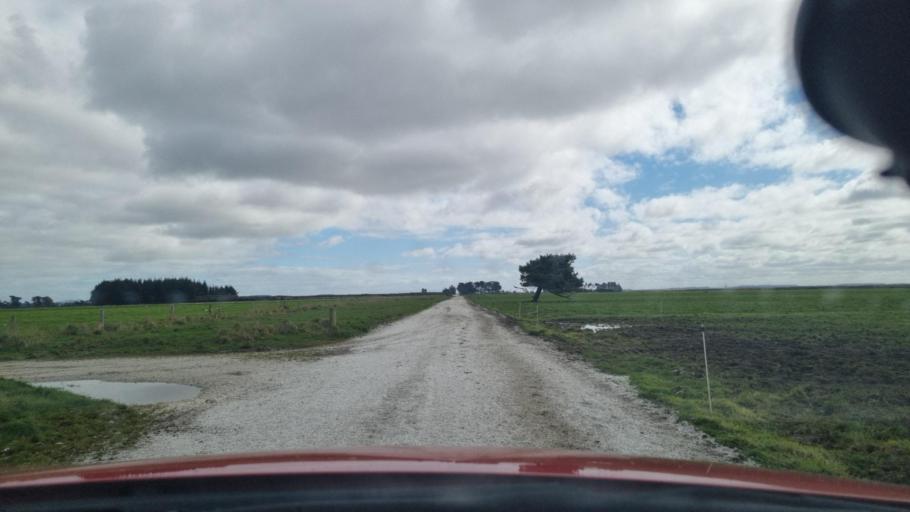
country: NZ
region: Southland
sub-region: Invercargill City
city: Bluff
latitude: -46.5637
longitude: 168.4969
